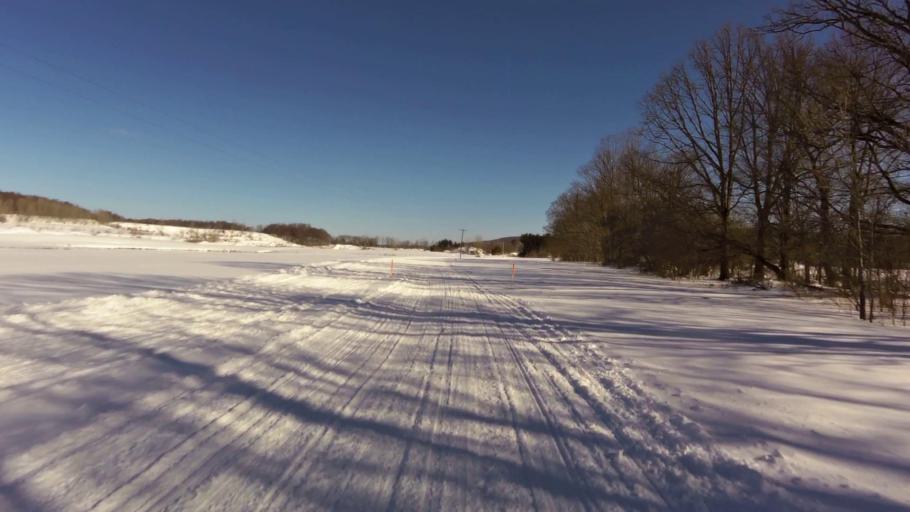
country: US
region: New York
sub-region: Cattaraugus County
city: Franklinville
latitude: 42.3648
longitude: -78.4649
